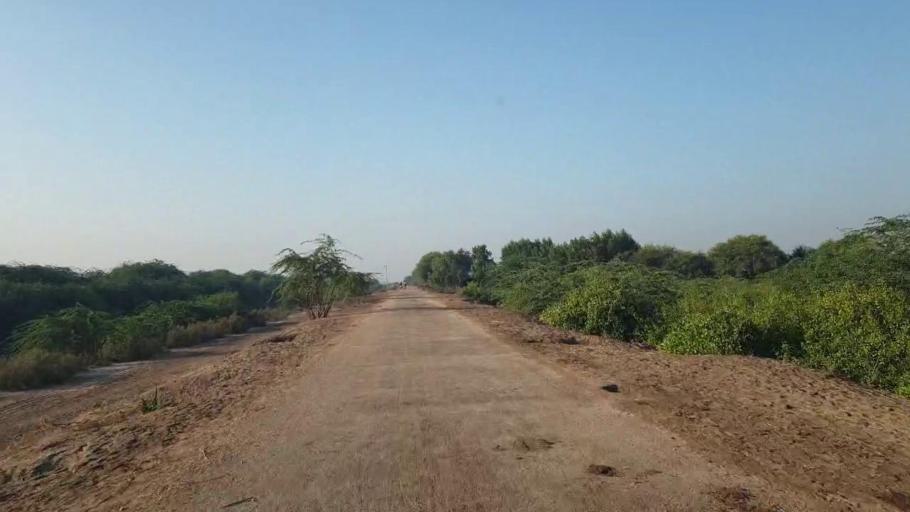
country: PK
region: Sindh
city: Badin
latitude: 24.5992
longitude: 68.7750
